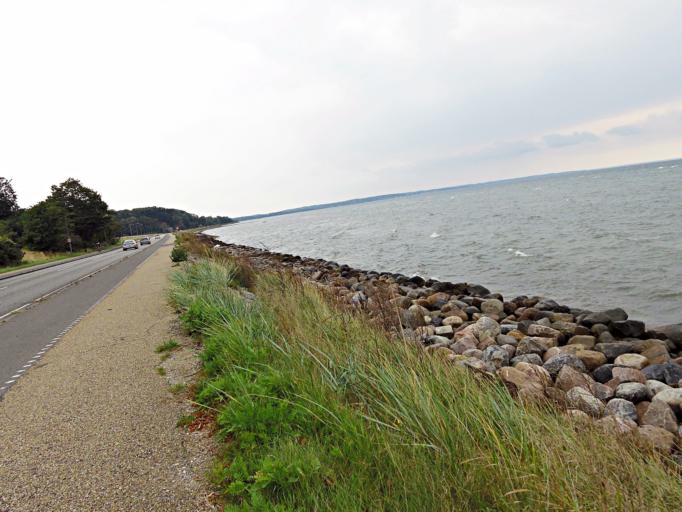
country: DK
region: Capital Region
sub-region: Fredensborg Kommune
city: Kokkedal
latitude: 55.9005
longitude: 12.5328
